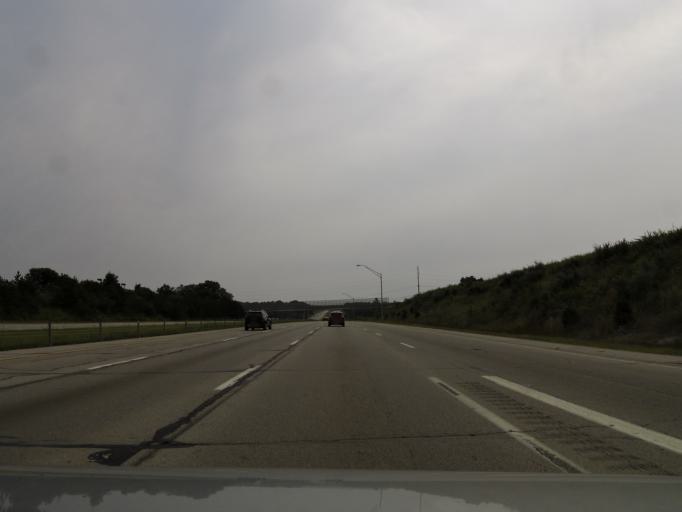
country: US
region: Ohio
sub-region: Montgomery County
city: Centerville
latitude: 39.6478
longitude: -84.1513
